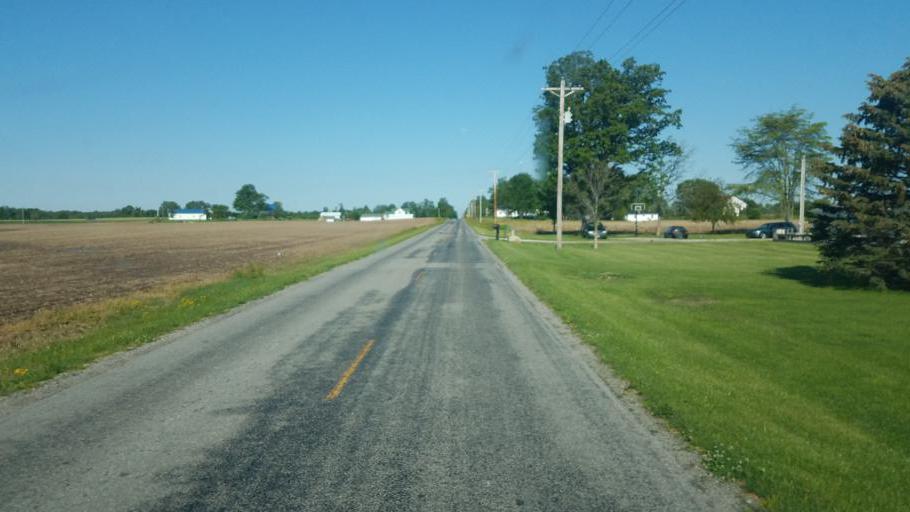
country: US
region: Ohio
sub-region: Hardin County
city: Kenton
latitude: 40.5806
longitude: -83.5518
